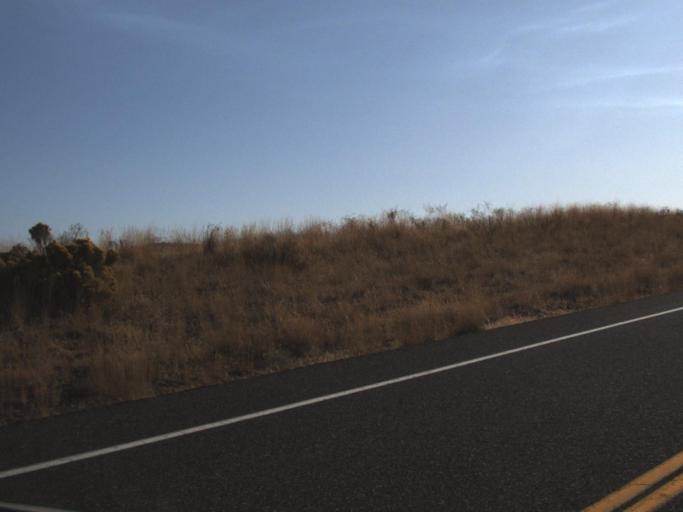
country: US
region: Washington
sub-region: Benton County
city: Highland
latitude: 46.1489
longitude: -119.1823
